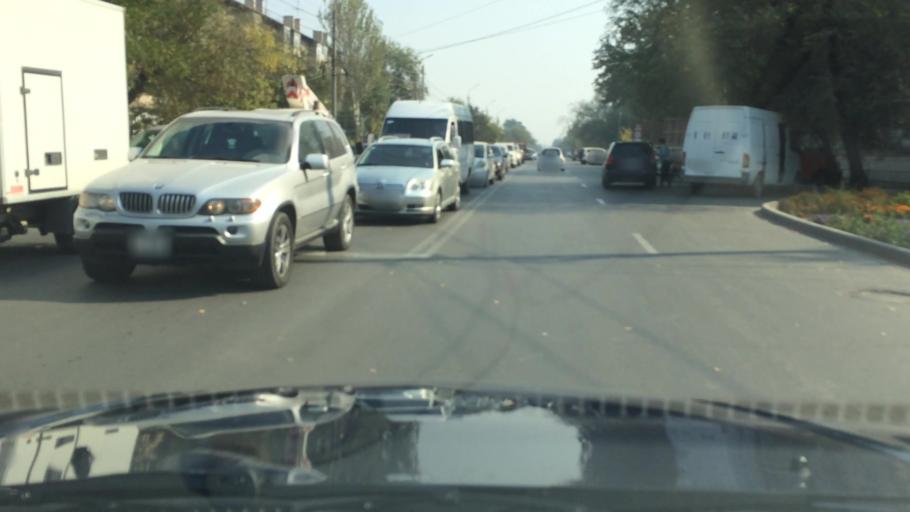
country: KG
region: Chuy
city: Lebedinovka
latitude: 42.8835
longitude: 74.6369
